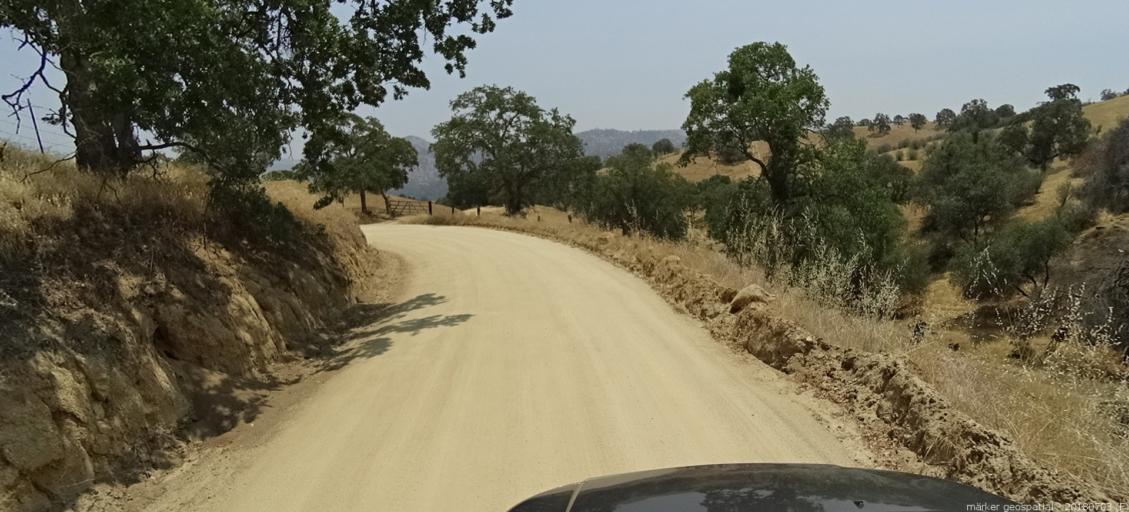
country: US
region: California
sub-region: Madera County
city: Yosemite Lakes
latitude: 37.0709
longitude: -119.6655
